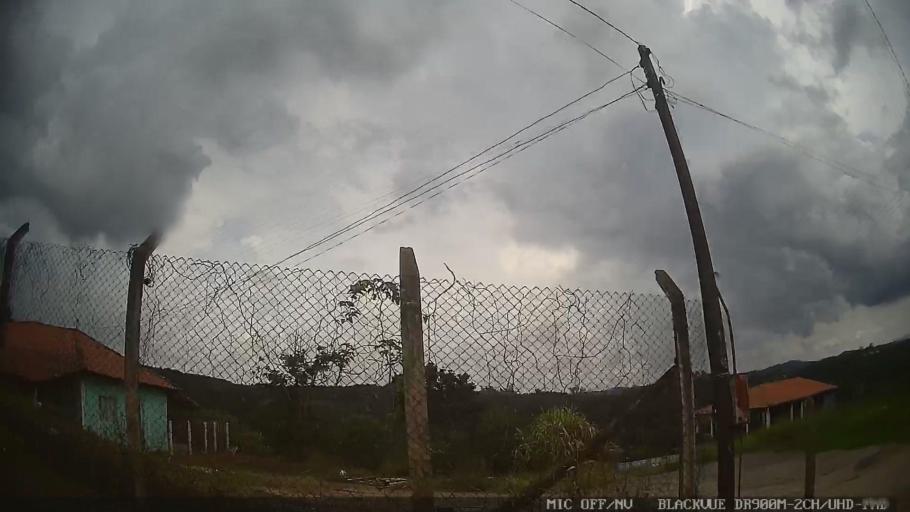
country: BR
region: Sao Paulo
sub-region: Aruja
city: Aruja
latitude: -23.4155
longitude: -46.2297
